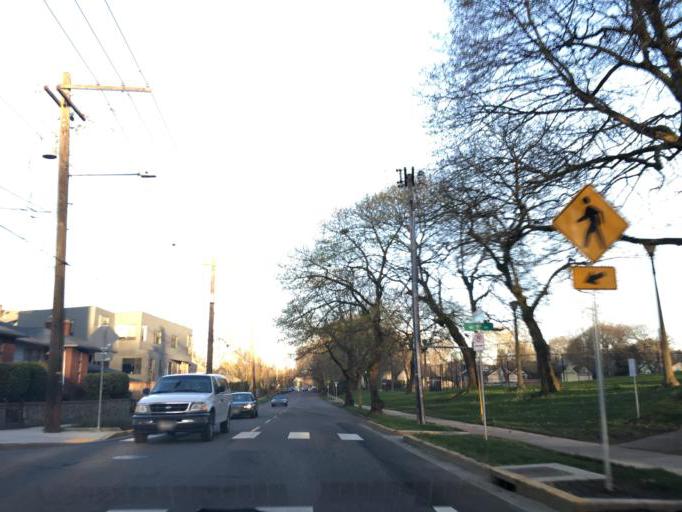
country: US
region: Oregon
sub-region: Multnomah County
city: Portland
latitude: 45.5482
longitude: -122.6570
